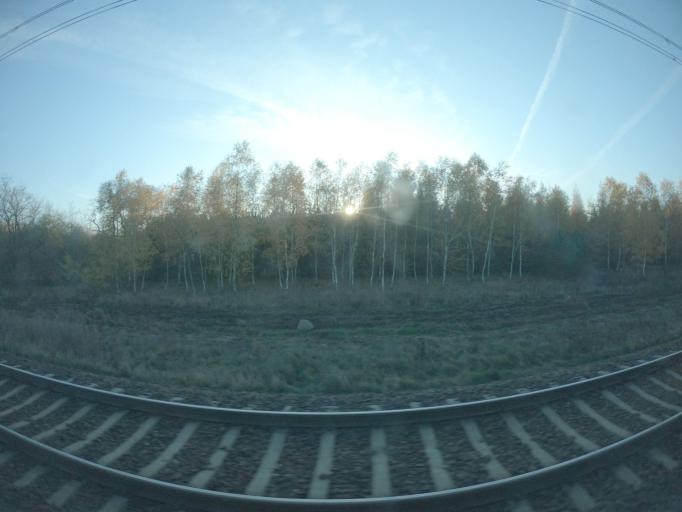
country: PL
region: Lubusz
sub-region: Powiat slubicki
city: Rzepin
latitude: 52.2890
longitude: 14.8912
